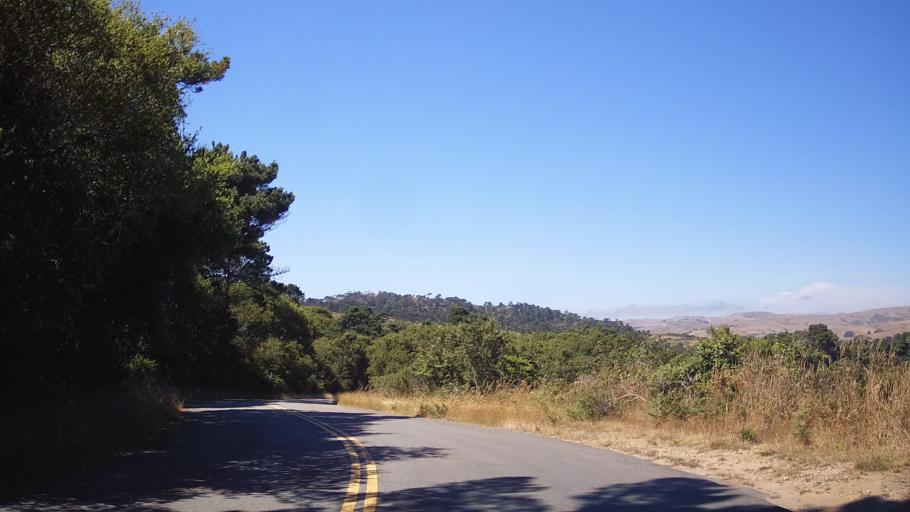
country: US
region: California
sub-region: Marin County
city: Inverness
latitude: 38.1248
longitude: -122.9017
